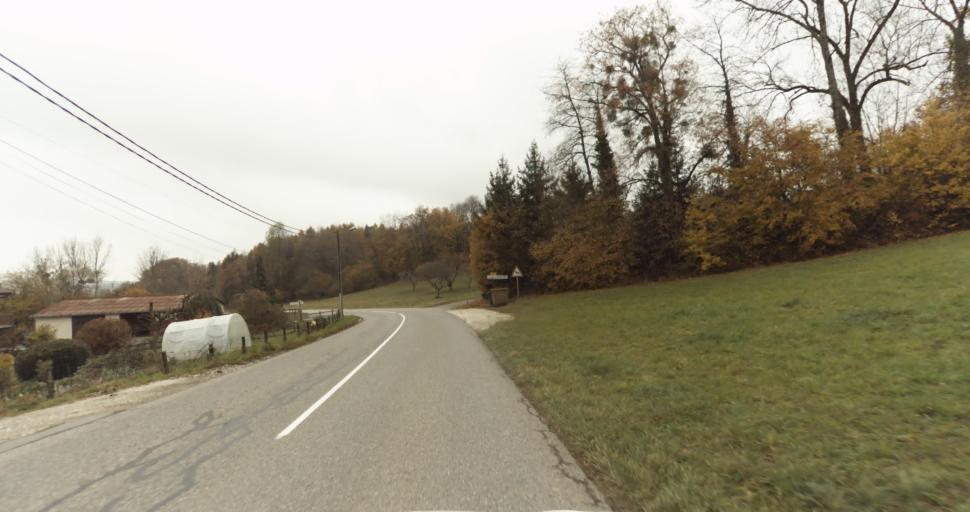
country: FR
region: Rhone-Alpes
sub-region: Departement de la Haute-Savoie
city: Viuz-la-Chiesaz
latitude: 45.8153
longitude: 6.0606
